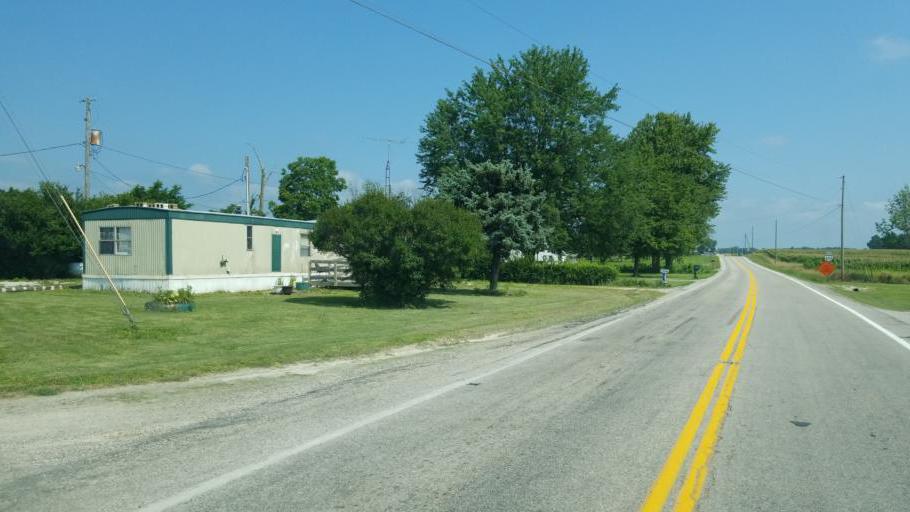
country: US
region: Ohio
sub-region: Crawford County
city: Galion
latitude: 40.8135
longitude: -82.8557
